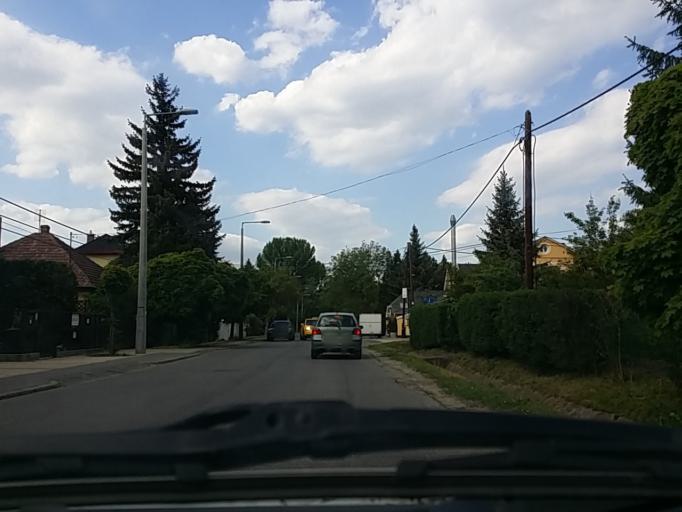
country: HU
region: Budapest
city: Budapest III. keruelet
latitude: 47.5760
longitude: 19.0466
